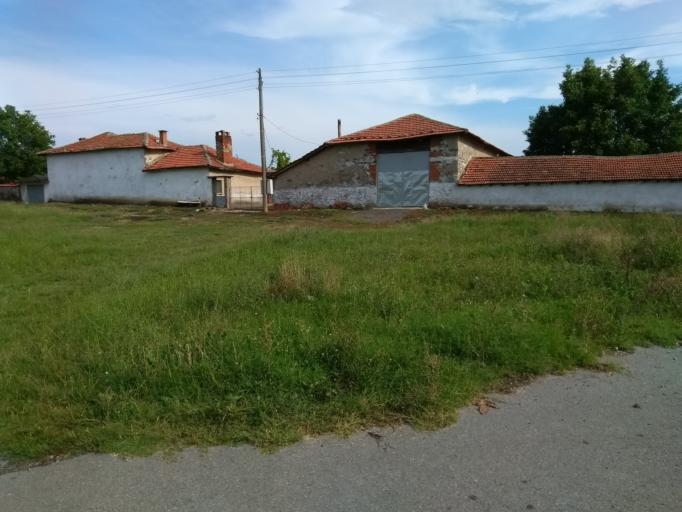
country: BG
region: Sliven
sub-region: Obshtina Sliven
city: Kermen
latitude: 42.4575
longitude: 26.1472
